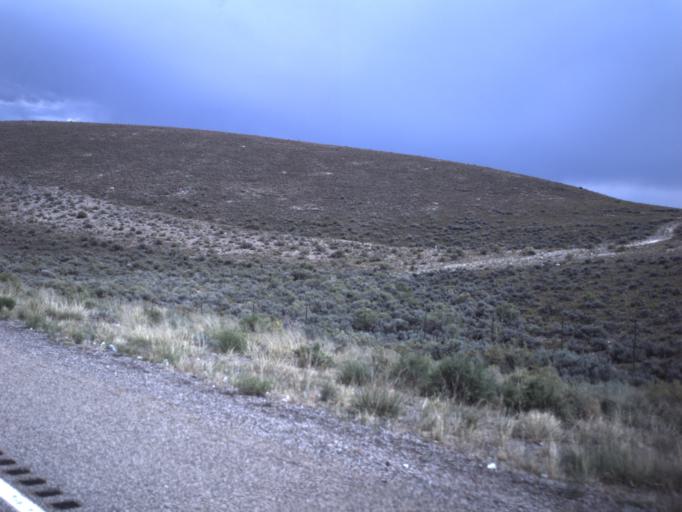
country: US
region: Utah
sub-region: Piute County
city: Junction
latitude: 38.2058
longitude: -112.2279
